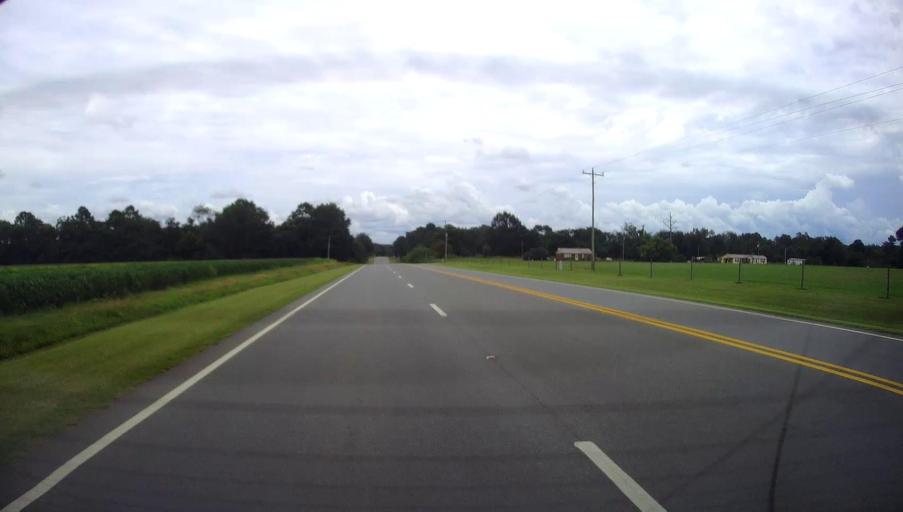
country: US
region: Georgia
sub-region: Macon County
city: Montezuma
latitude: 32.2931
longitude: -83.9538
